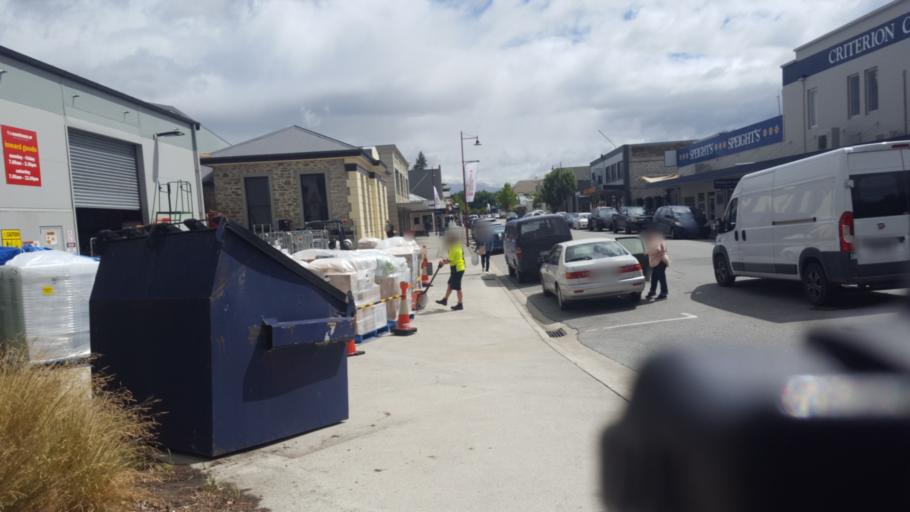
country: NZ
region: Otago
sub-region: Queenstown-Lakes District
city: Wanaka
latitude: -45.2584
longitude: 169.3930
